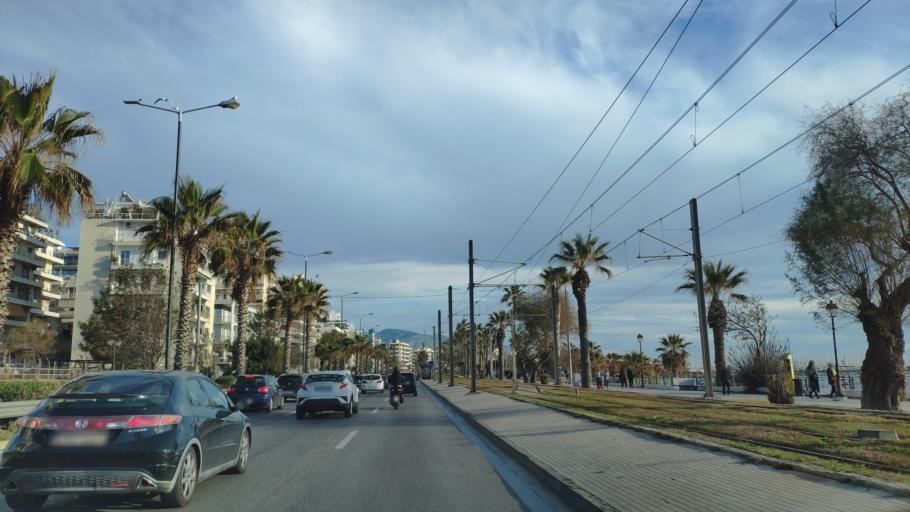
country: GR
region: Attica
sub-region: Nomarchia Athinas
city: Palaio Faliro
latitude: 37.9188
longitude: 23.6971
